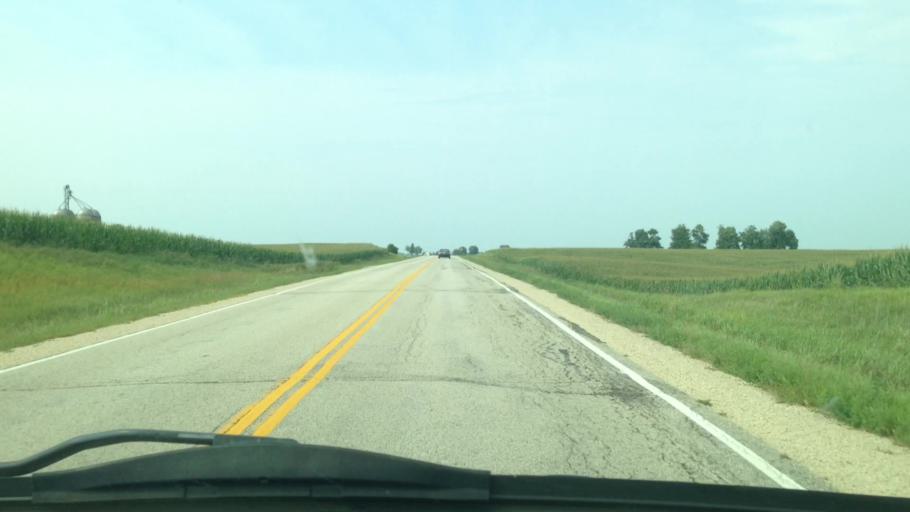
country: US
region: Minnesota
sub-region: Winona County
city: Saint Charles
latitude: 43.8788
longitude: -91.9594
